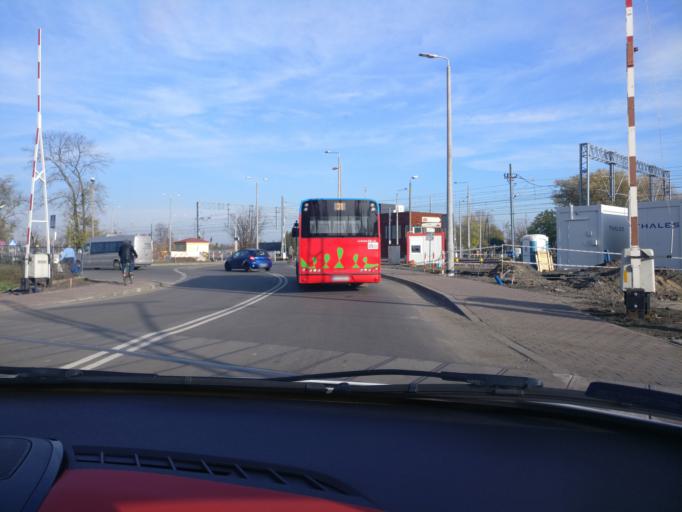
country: PL
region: Lublin Voivodeship
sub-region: Powiat rycki
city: Deblin
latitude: 51.5754
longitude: 21.8375
